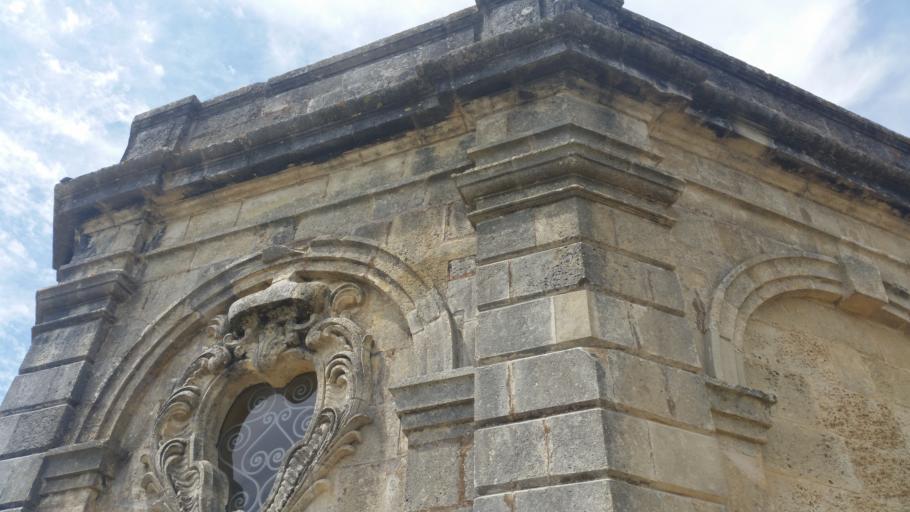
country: FR
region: Poitou-Charentes
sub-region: Departement de la Charente-Maritime
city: Port-des-Barques
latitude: 45.9528
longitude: -1.0534
